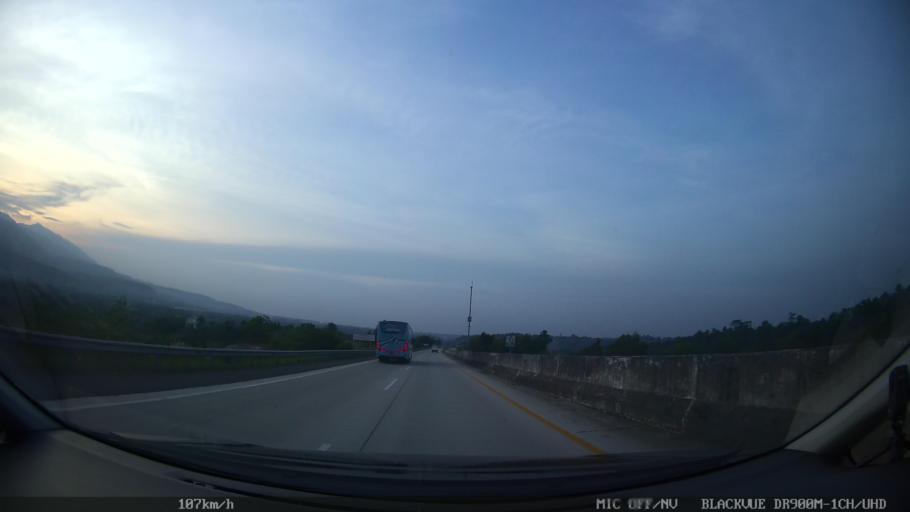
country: ID
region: Lampung
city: Penengahan
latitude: -5.7900
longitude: 105.7254
